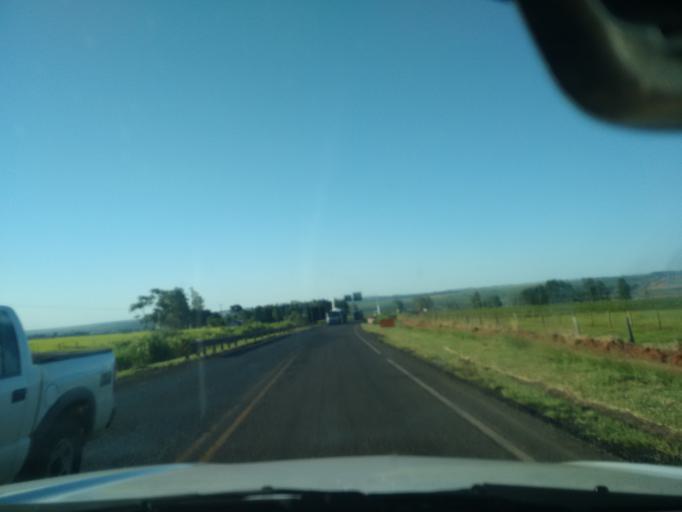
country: BR
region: Mato Grosso do Sul
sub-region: Eldorado
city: Eldorado
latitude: -23.8562
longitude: -54.3356
